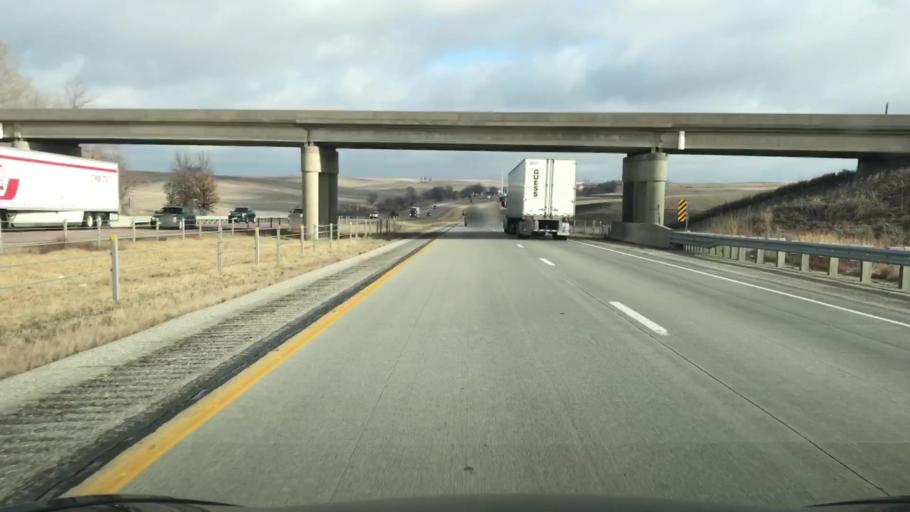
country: US
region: Iowa
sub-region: Guthrie County
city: Guthrie Center
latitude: 41.4952
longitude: -94.5863
